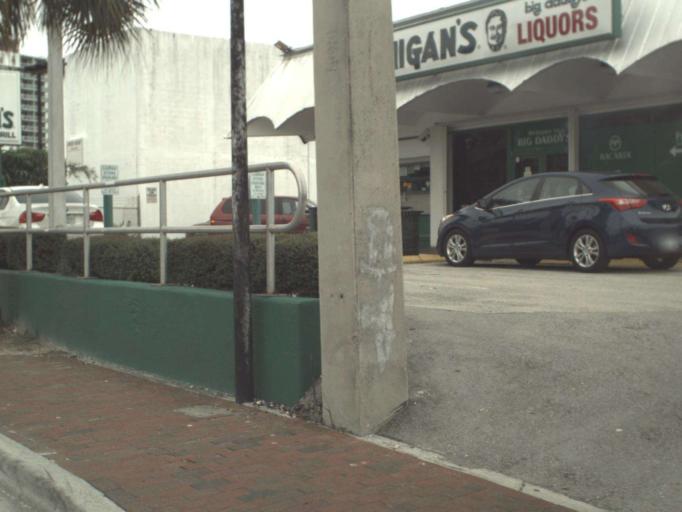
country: US
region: Florida
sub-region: Miami-Dade County
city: Biscayne Park
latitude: 25.8975
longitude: -80.1612
